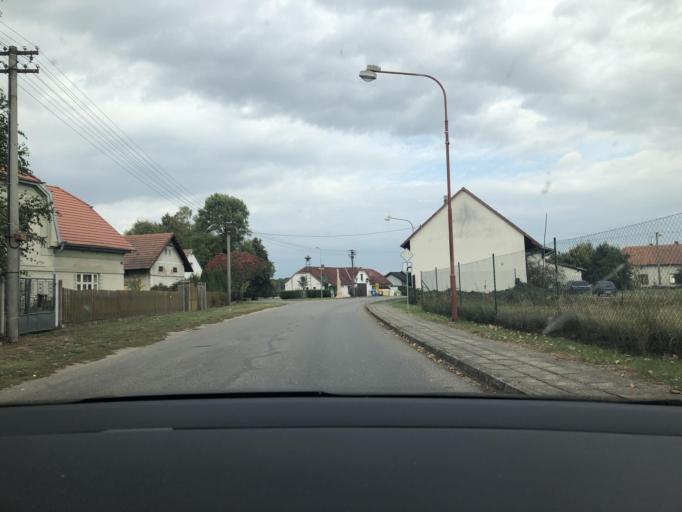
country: CZ
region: Pardubicky
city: Recany nad Labem
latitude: 50.0863
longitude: 15.4781
